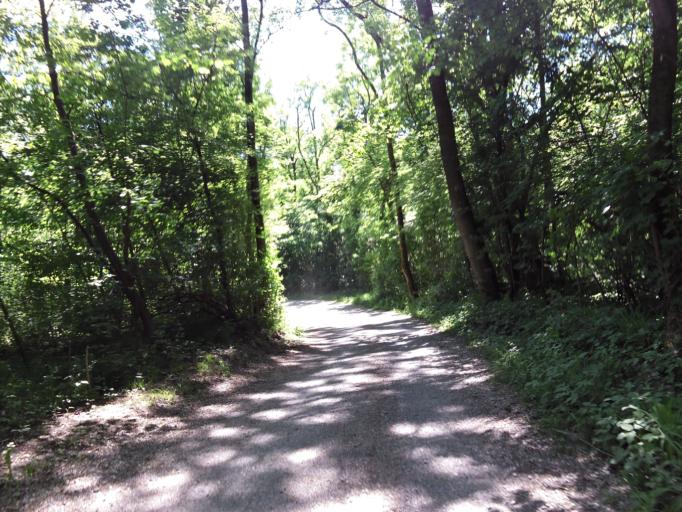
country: DE
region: Bavaria
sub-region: Upper Bavaria
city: Unterfoehring
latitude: 48.1943
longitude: 11.6323
